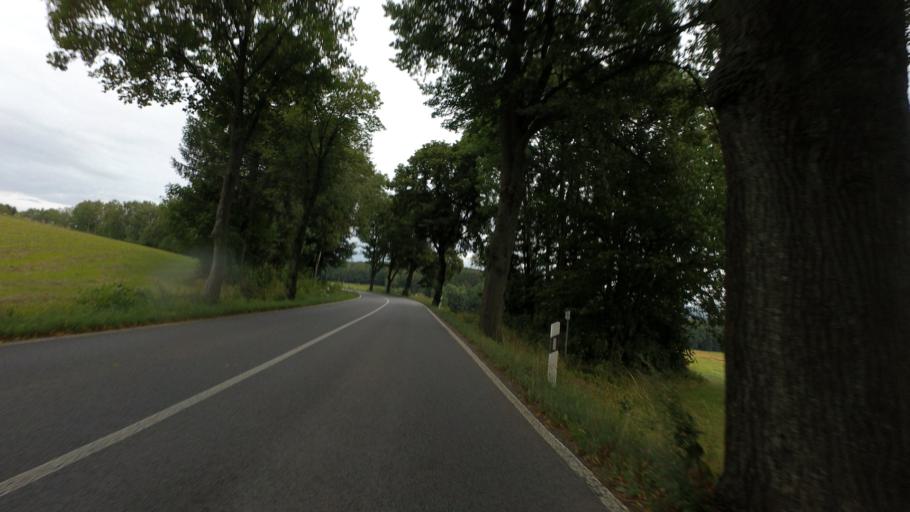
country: DE
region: Saxony
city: Berthelsdorf
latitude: 51.0818
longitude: 14.2016
